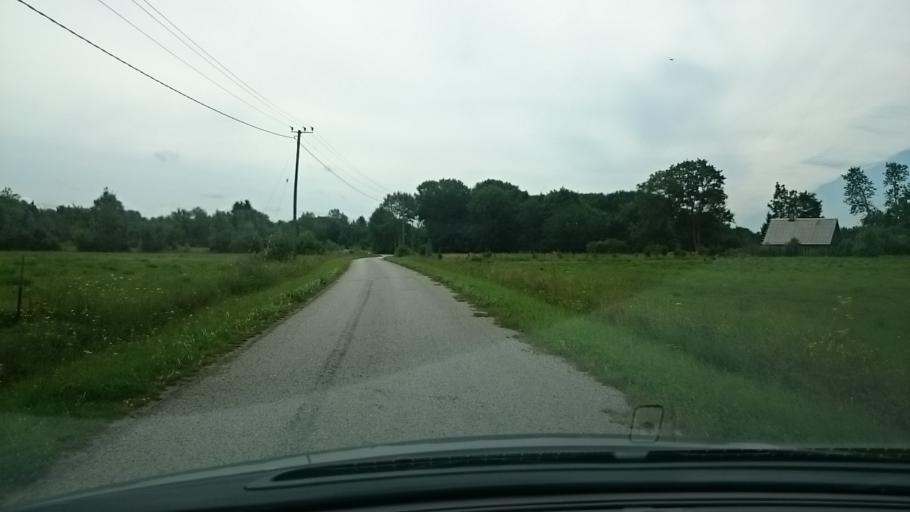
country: EE
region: Laeaene
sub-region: Ridala Parish
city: Uuemoisa
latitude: 58.9914
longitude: 23.6626
